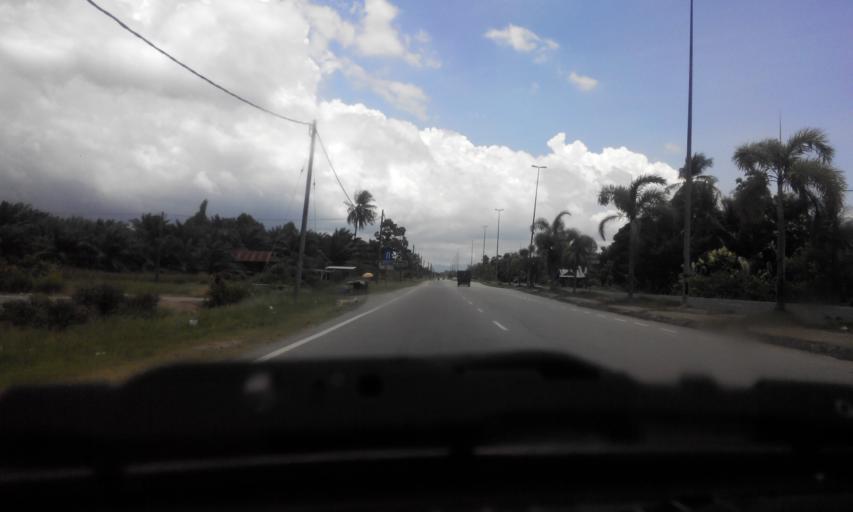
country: MY
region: Perak
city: Parit Buntar
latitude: 5.1251
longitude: 100.5147
